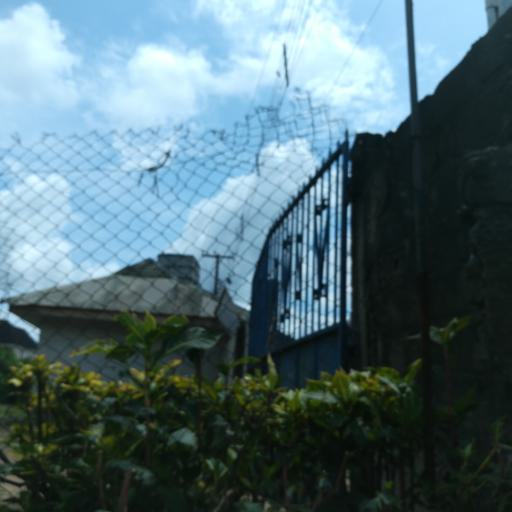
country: NG
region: Rivers
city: Port Harcourt
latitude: 4.7763
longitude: 7.0428
